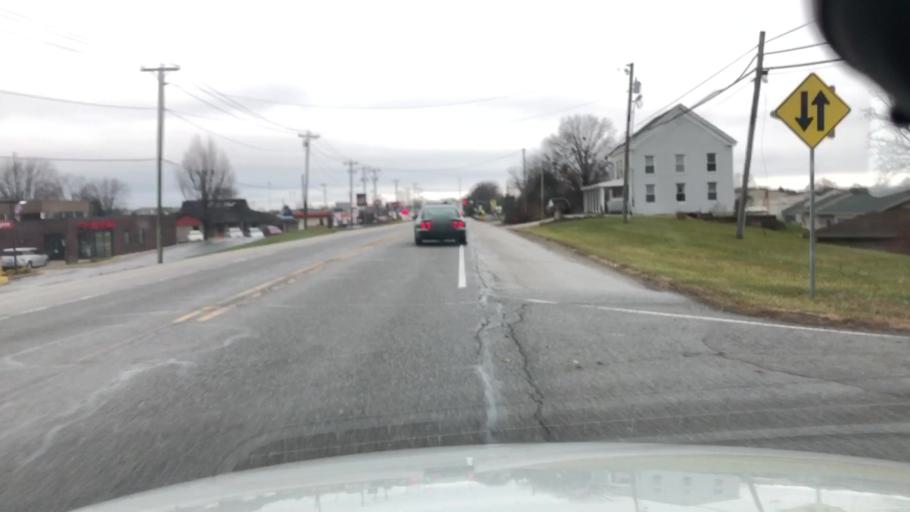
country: US
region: Indiana
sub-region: Allen County
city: New Haven
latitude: 41.0668
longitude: -85.0067
